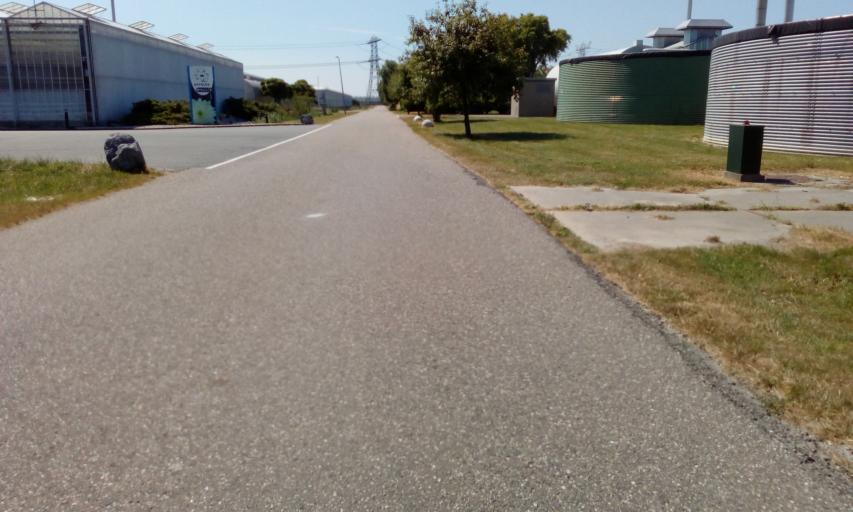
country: NL
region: South Holland
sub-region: Gemeente Westland
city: Naaldwijk
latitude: 51.9875
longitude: 4.2244
